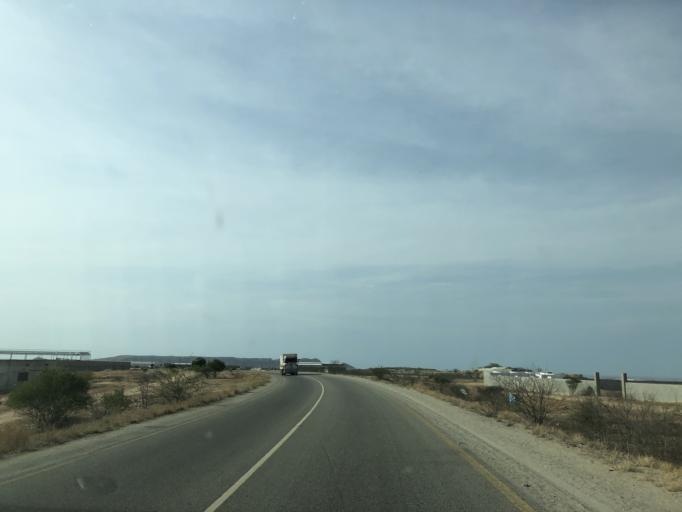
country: AO
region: Benguela
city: Benguela
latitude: -12.6940
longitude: 13.3453
